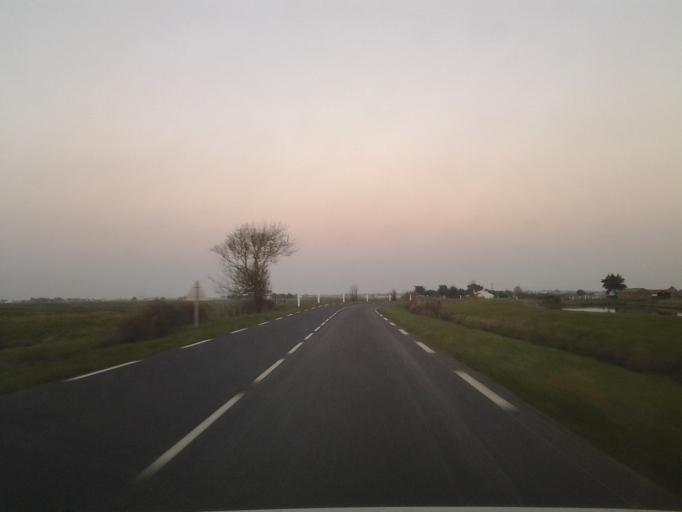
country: FR
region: Pays de la Loire
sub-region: Departement de la Vendee
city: Beauvoir-sur-Mer
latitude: 46.9167
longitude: -2.0752
